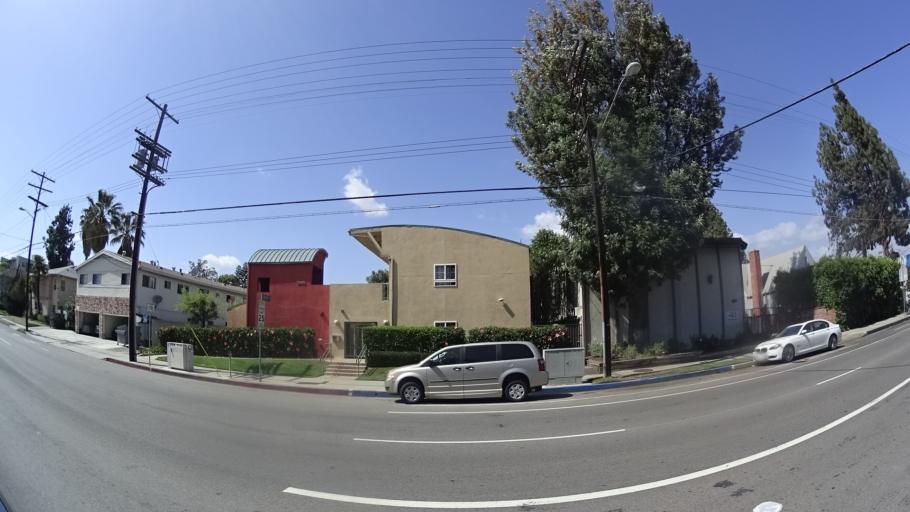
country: US
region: California
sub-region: Los Angeles County
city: North Hollywood
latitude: 34.1722
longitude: -118.3981
